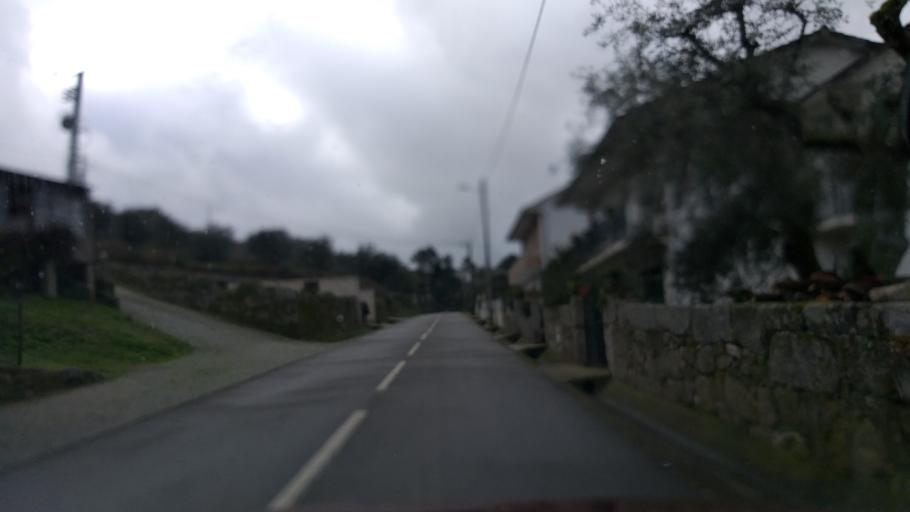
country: PT
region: Guarda
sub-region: Celorico da Beira
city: Celorico da Beira
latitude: 40.7085
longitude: -7.4310
